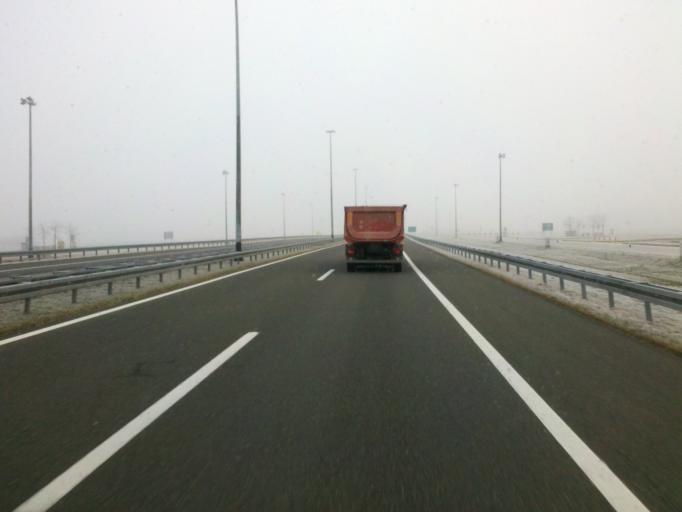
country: HR
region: Varazdinska
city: Jalzabet
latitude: 46.2843
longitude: 16.4550
